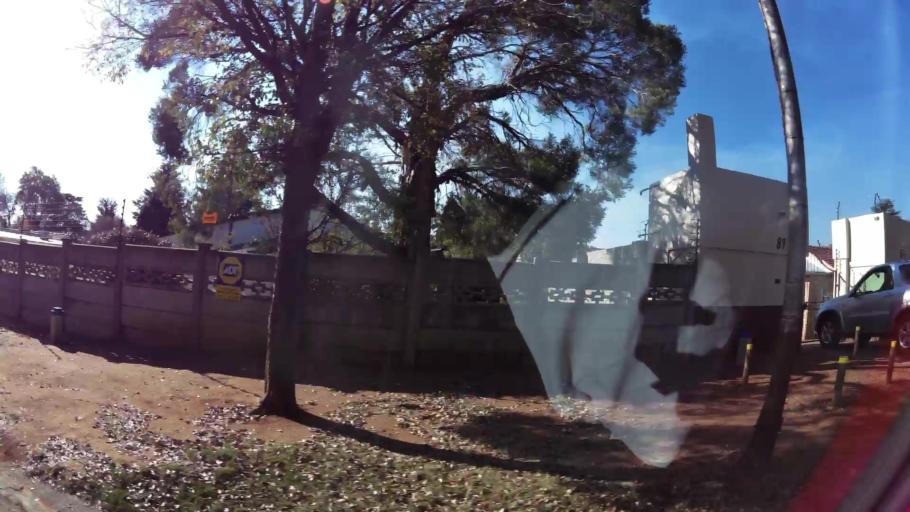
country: ZA
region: Gauteng
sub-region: City of Johannesburg Metropolitan Municipality
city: Roodepoort
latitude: -26.0919
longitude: 27.9744
